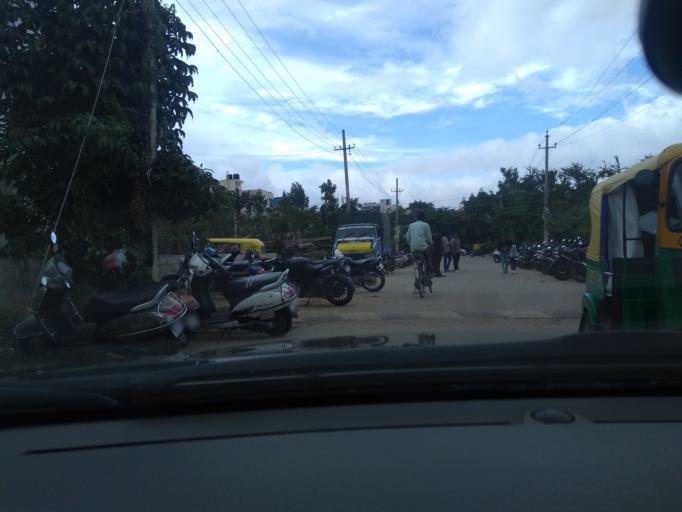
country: IN
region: Karnataka
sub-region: Bangalore Urban
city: Bangalore
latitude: 13.0057
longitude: 77.6603
